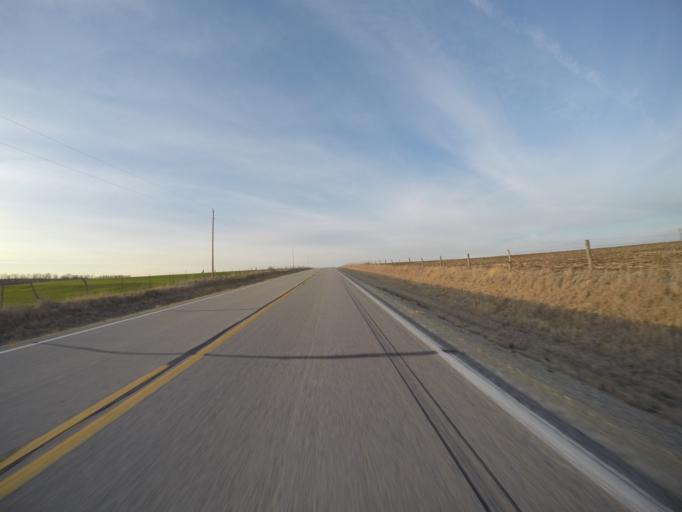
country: US
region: Kansas
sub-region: Clay County
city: Clay Center
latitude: 39.3886
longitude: -96.8492
